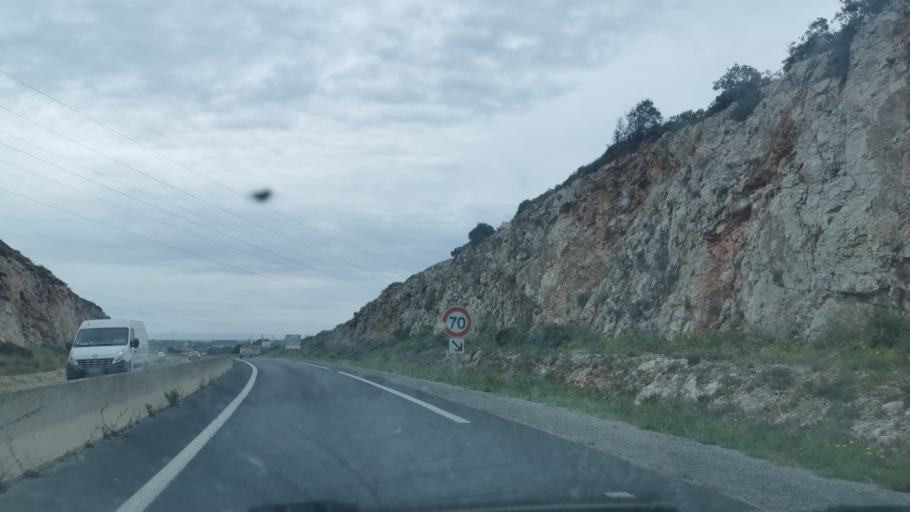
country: FR
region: Languedoc-Roussillon
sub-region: Departement de l'Herault
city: Balaruc-le-Vieux
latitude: 43.4502
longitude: 3.7064
